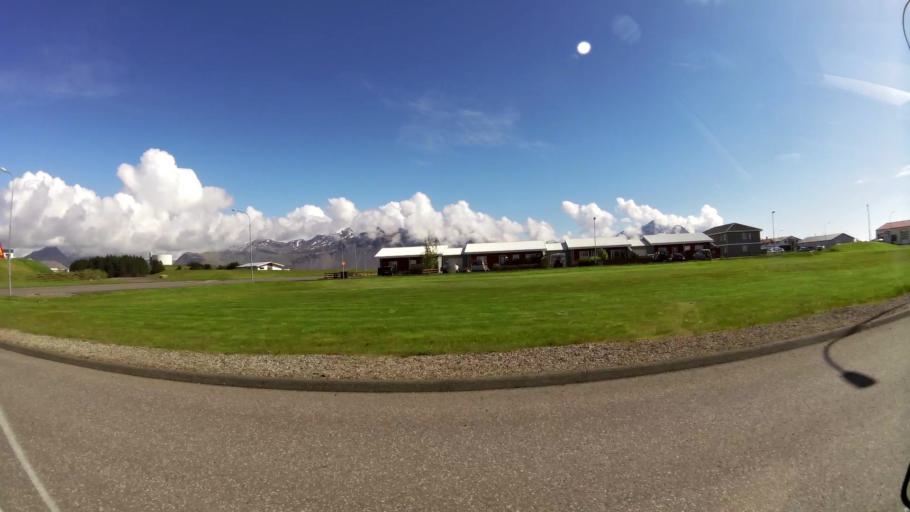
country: IS
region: East
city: Hoefn
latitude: 64.2535
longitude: -15.2053
